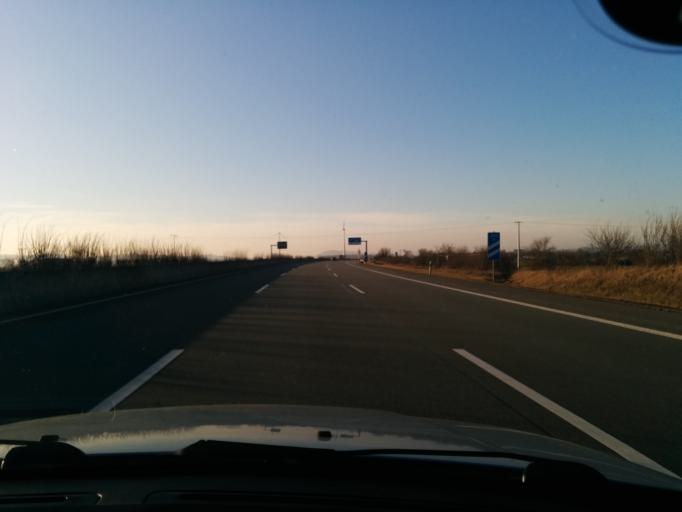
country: DE
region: Thuringia
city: Horselgau
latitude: 50.9080
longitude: 10.5958
